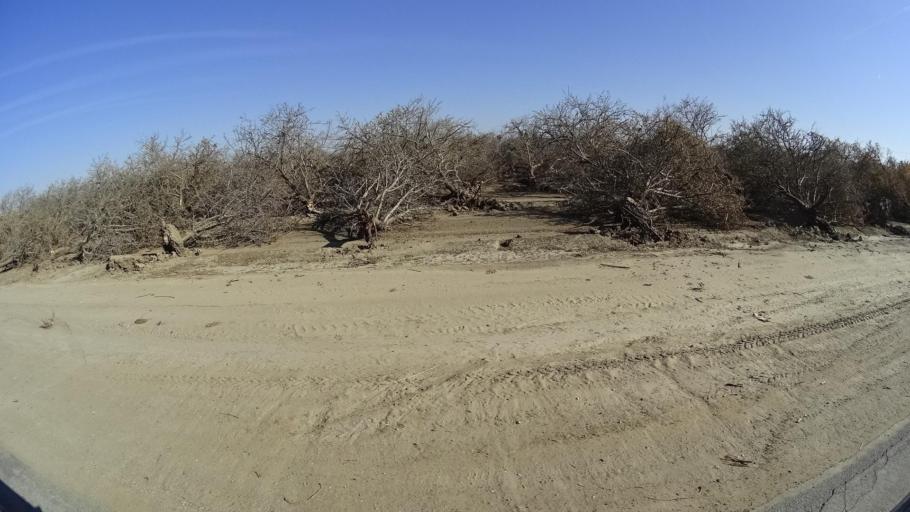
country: US
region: California
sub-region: Kern County
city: Wasco
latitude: 35.6606
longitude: -119.3486
